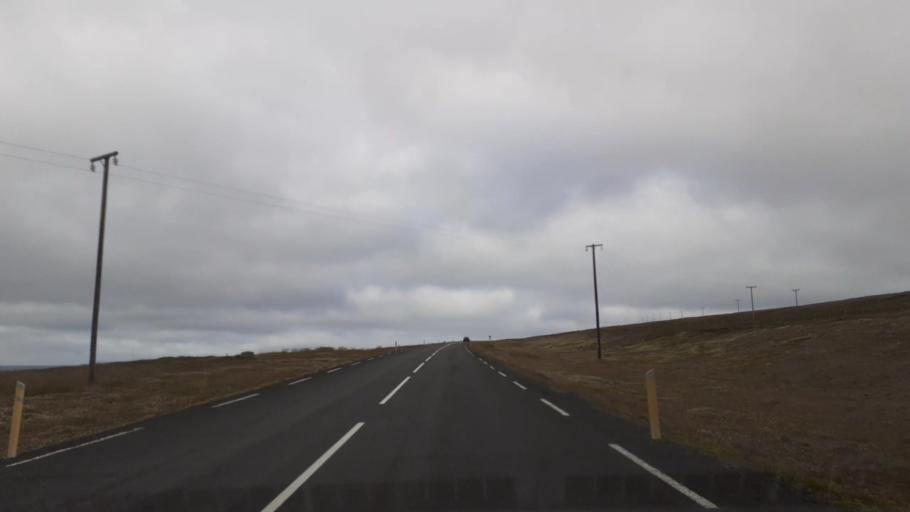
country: IS
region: Northeast
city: Husavik
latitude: 66.1850
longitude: -17.1538
